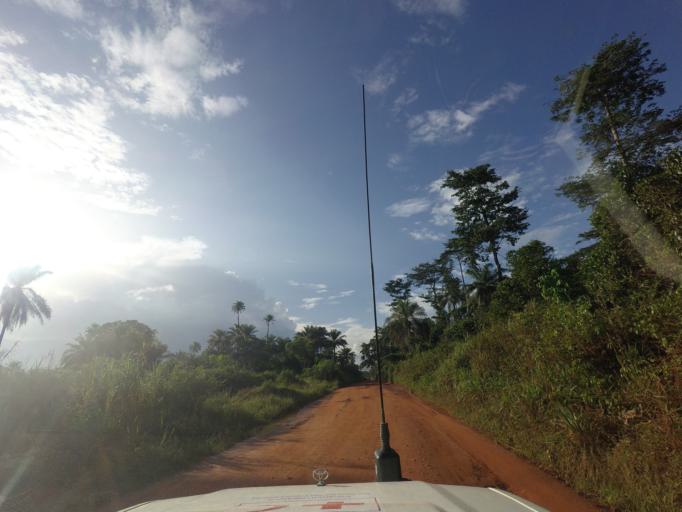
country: GN
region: Nzerekore
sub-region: Nzerekore Prefecture
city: Nzerekore
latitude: 7.7116
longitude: -8.8196
